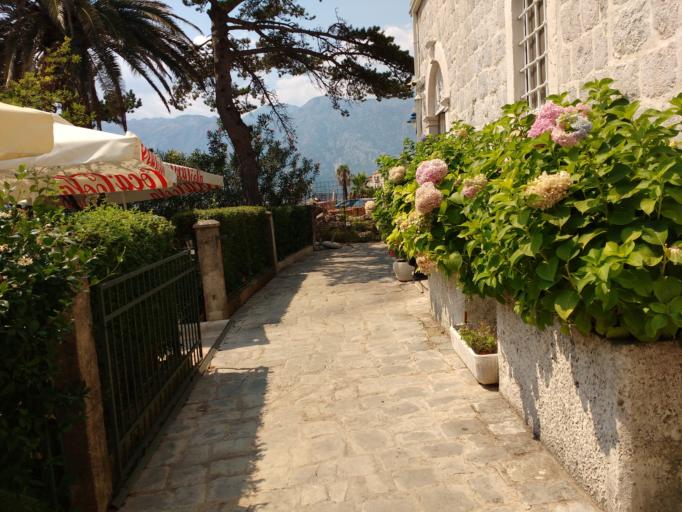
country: ME
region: Kotor
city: Risan
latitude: 42.4864
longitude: 18.6979
